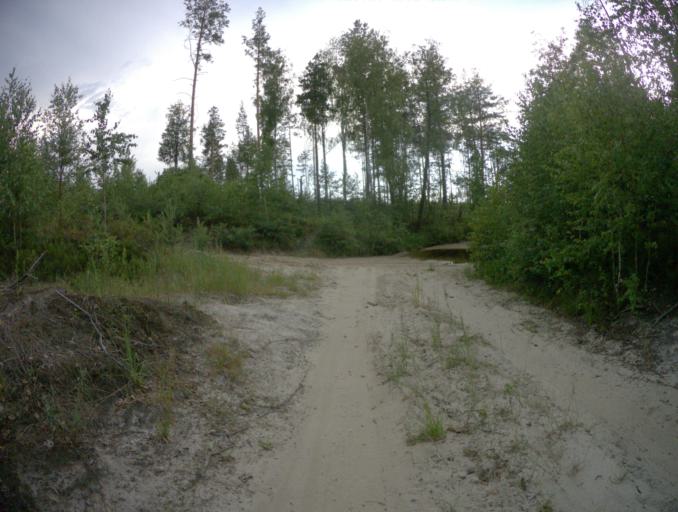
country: RU
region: Ivanovo
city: Talitsy
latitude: 56.4269
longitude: 42.2954
